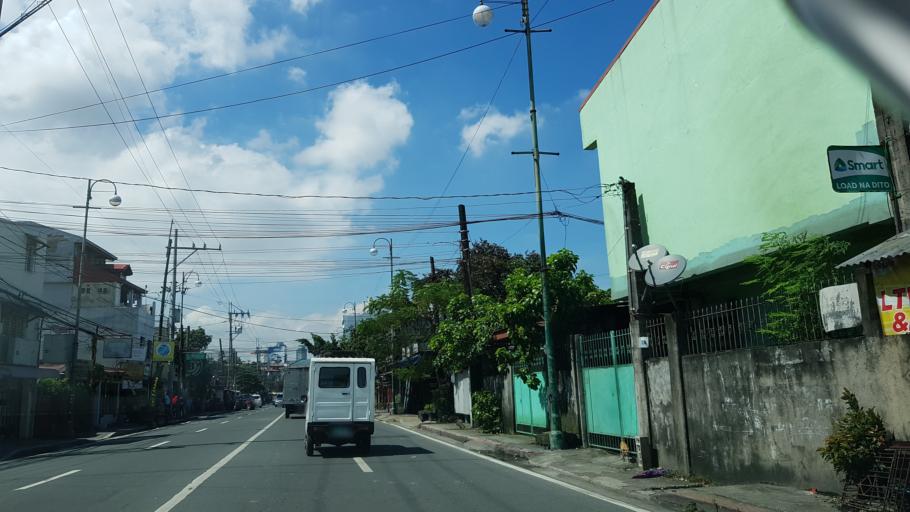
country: PH
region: Calabarzon
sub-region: Province of Rizal
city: Pateros
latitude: 14.5499
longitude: 121.0637
